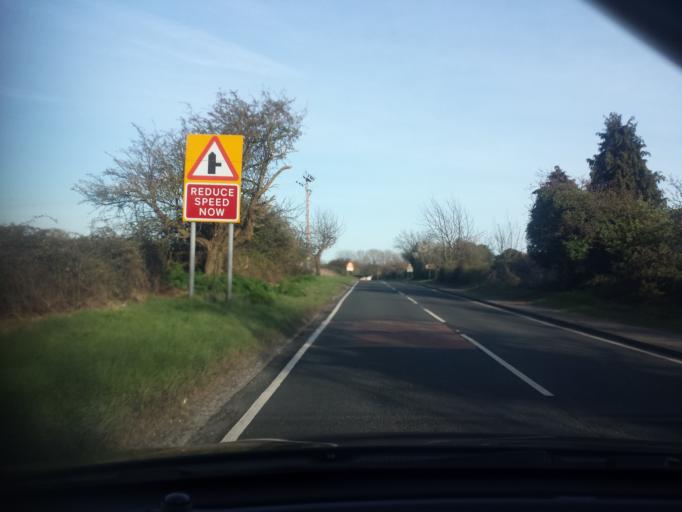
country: GB
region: England
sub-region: Essex
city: Saint Osyth
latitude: 51.8027
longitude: 1.0892
